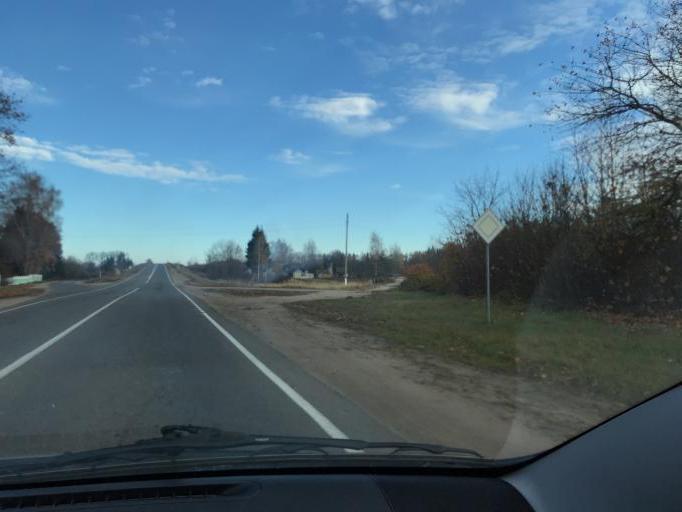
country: BY
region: Vitebsk
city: Haradok
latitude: 55.4956
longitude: 29.9669
